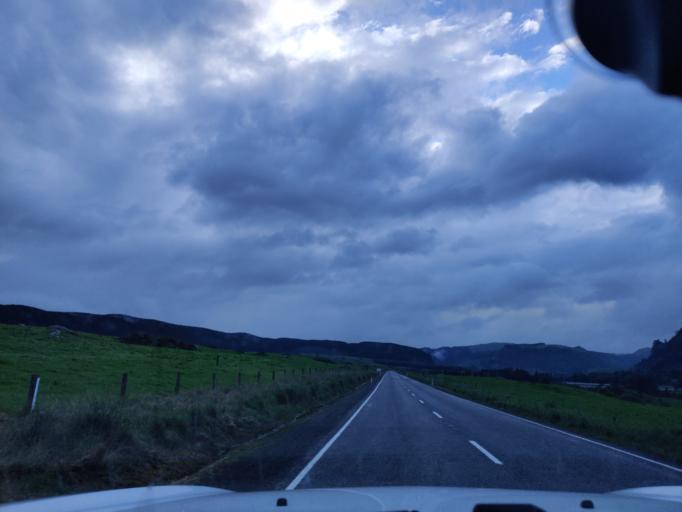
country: NZ
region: Waikato
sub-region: South Waikato District
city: Tokoroa
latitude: -38.4097
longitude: 175.7990
